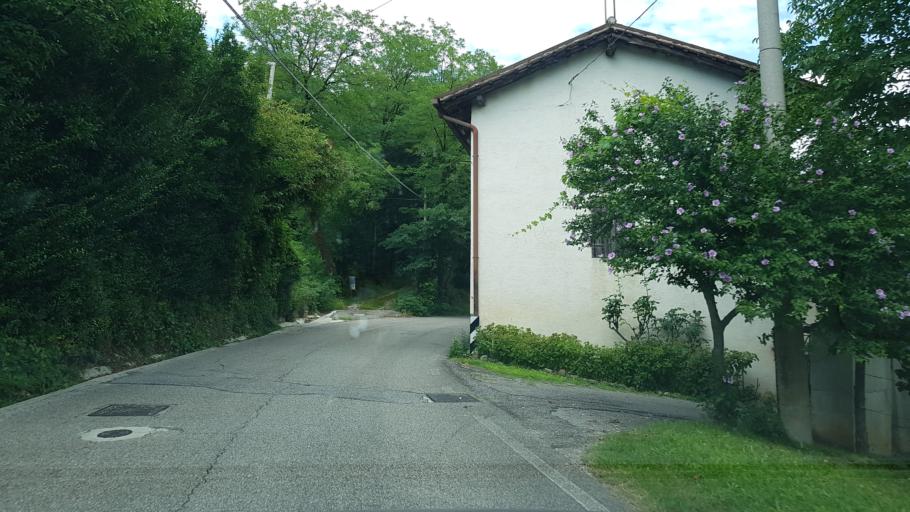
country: IT
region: Friuli Venezia Giulia
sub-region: Provincia di Udine
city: Prepotto
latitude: 46.0559
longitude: 13.4937
